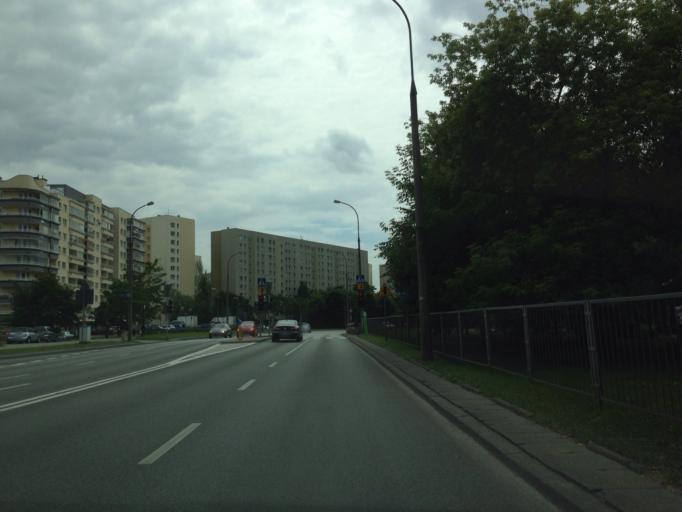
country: PL
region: Masovian Voivodeship
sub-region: Warszawa
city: Bemowo
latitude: 52.2526
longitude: 20.9240
